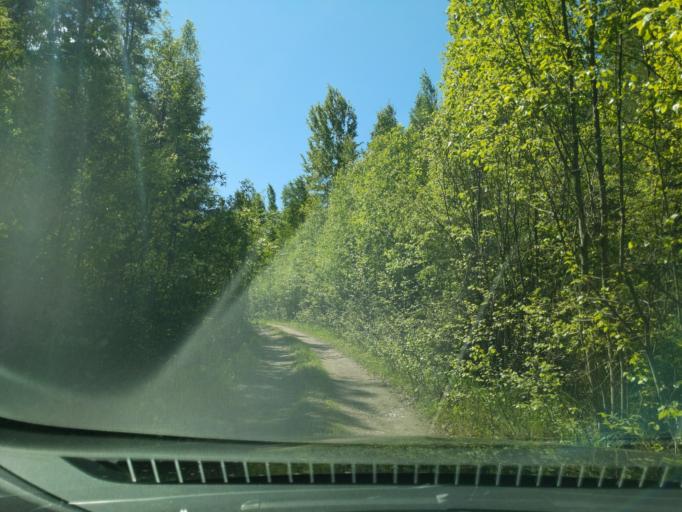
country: FI
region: Paijanne Tavastia
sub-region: Lahti
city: Lahti
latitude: 61.0481
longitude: 25.6942
